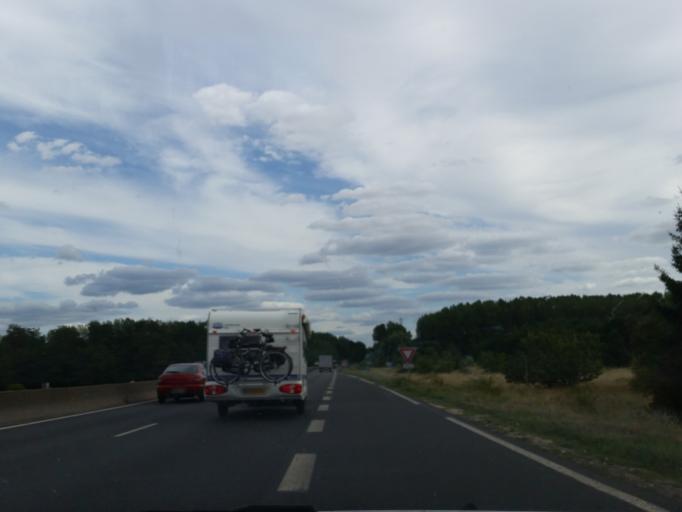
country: FR
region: Centre
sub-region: Departement du Loir-et-Cher
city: Vineuil
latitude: 47.5892
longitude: 1.3600
